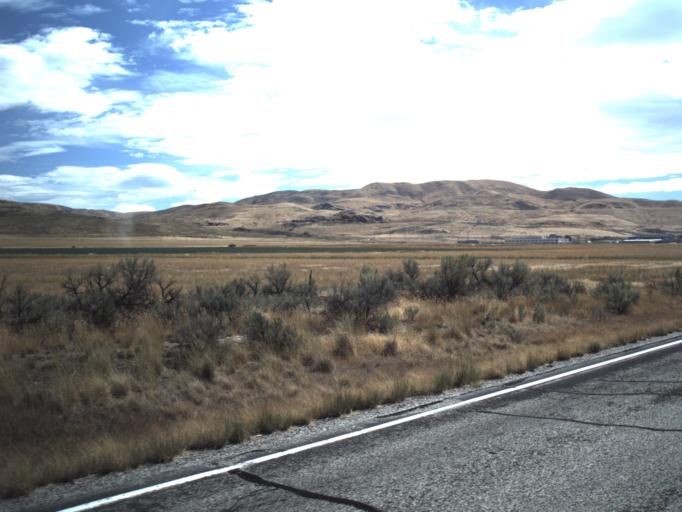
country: US
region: Utah
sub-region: Box Elder County
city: Tremonton
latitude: 41.7332
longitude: -112.4340
